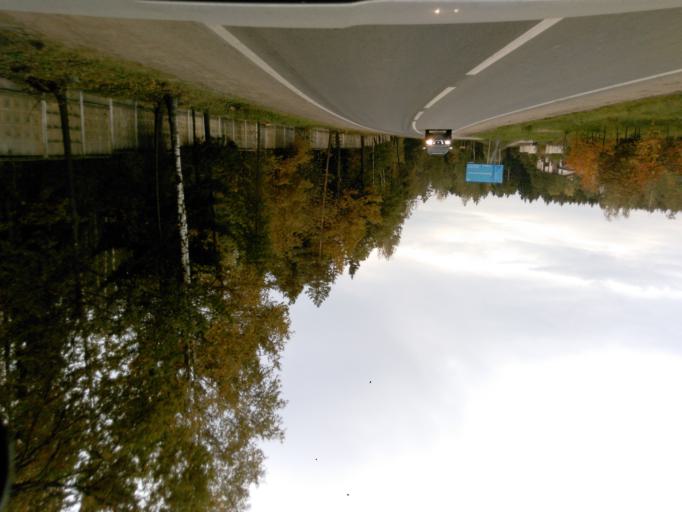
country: RU
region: Moskovskaya
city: Andreyevka
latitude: 55.9777
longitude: 37.1188
